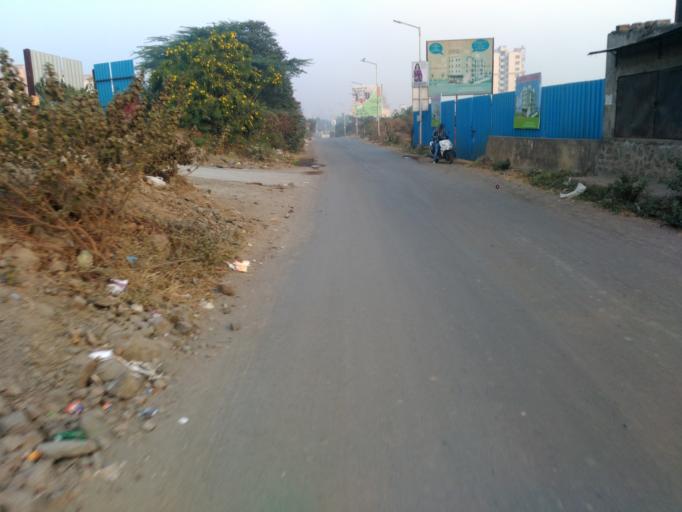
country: IN
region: Maharashtra
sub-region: Pune Division
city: Pune
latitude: 18.4417
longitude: 73.8865
